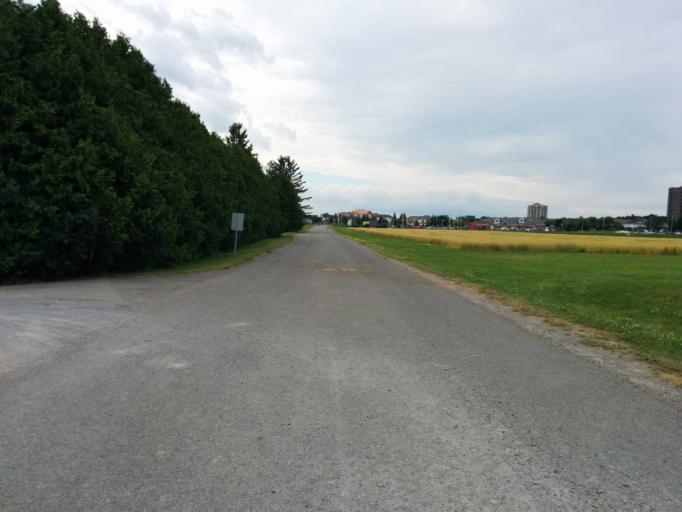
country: CA
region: Ontario
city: Ottawa
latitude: 45.3715
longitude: -75.7272
